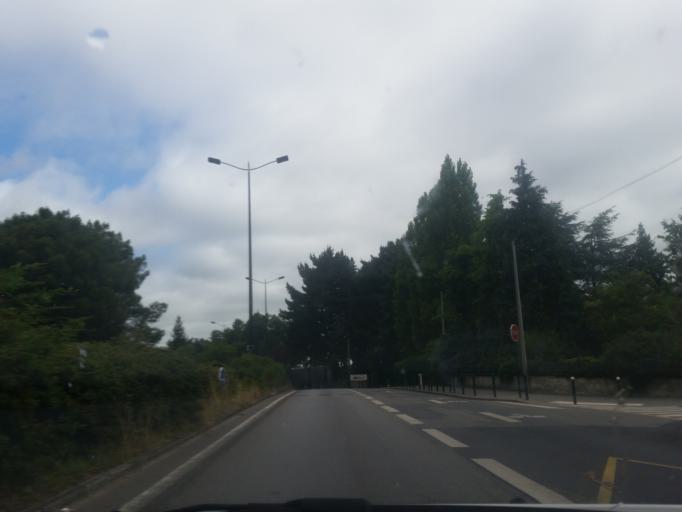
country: FR
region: Pays de la Loire
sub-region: Departement de la Loire-Atlantique
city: Nantes
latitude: 47.2534
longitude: -1.5529
